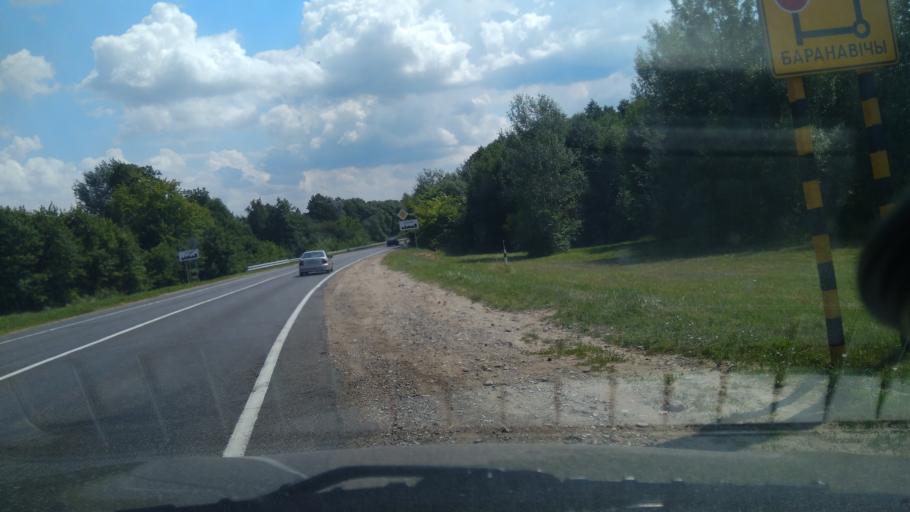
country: BY
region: Brest
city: Lyakhavichy
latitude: 53.1130
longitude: 26.1650
